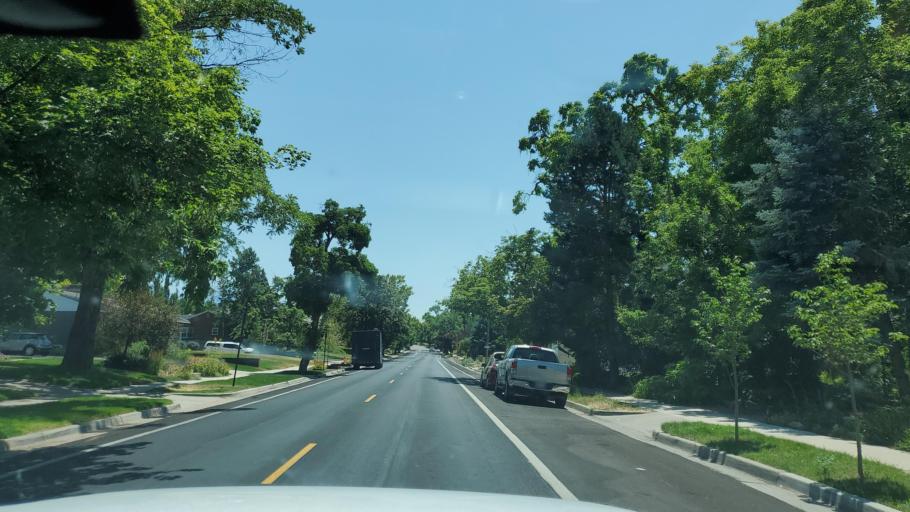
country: US
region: Utah
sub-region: Salt Lake County
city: Willard
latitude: 40.7220
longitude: -111.8309
